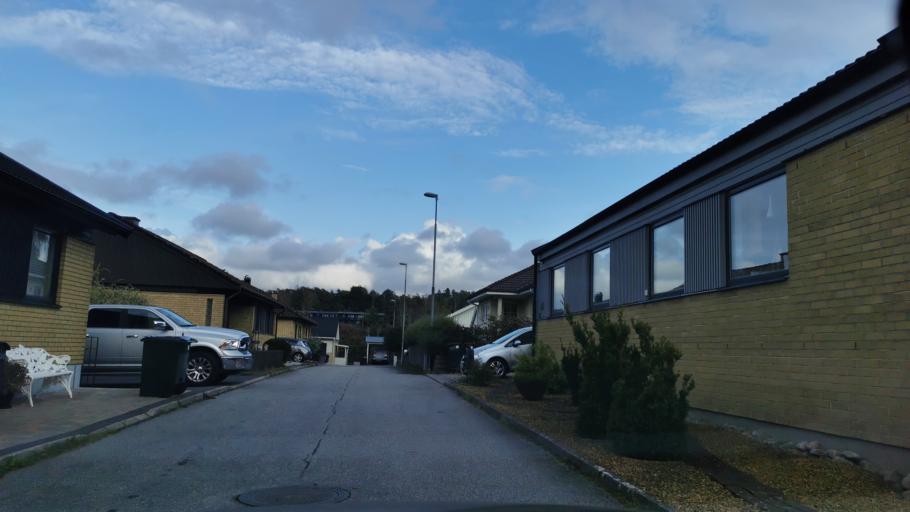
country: SE
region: Vaestra Goetaland
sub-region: Partille Kommun
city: Partille
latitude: 57.7143
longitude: 12.0751
